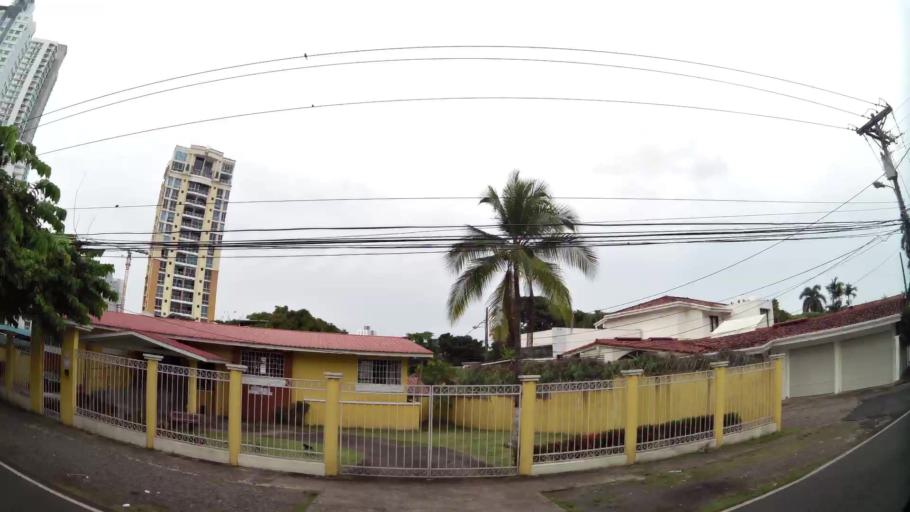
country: PA
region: Panama
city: Panama
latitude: 9.0033
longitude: -79.5049
